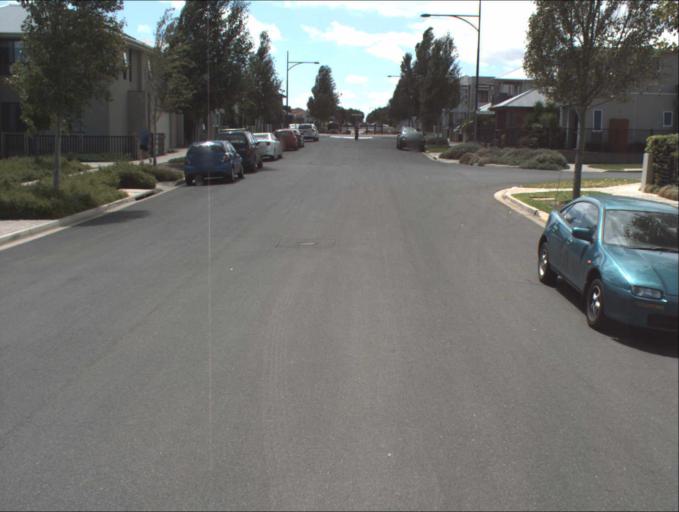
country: AU
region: South Australia
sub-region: Port Adelaide Enfield
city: Klemzig
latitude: -34.8597
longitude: 138.6328
